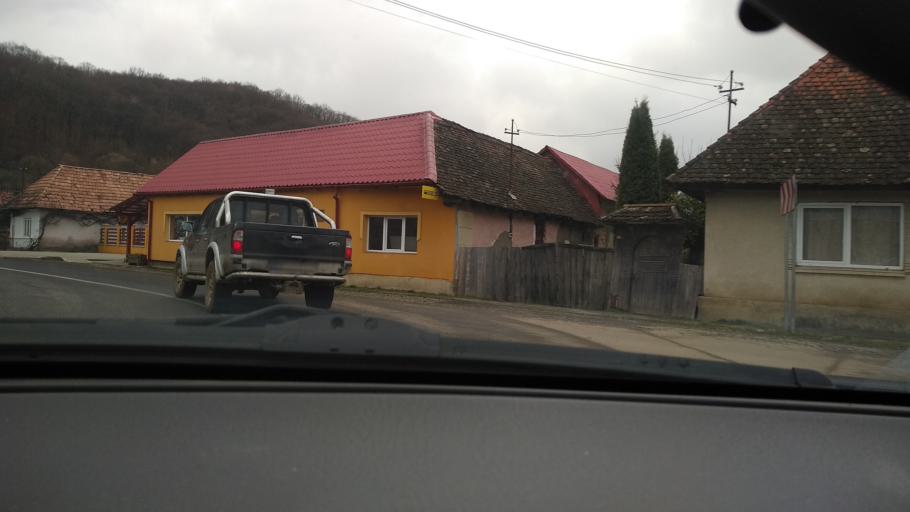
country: RO
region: Mures
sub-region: Comuna Bereni
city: Bereni
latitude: 46.5567
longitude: 24.8675
